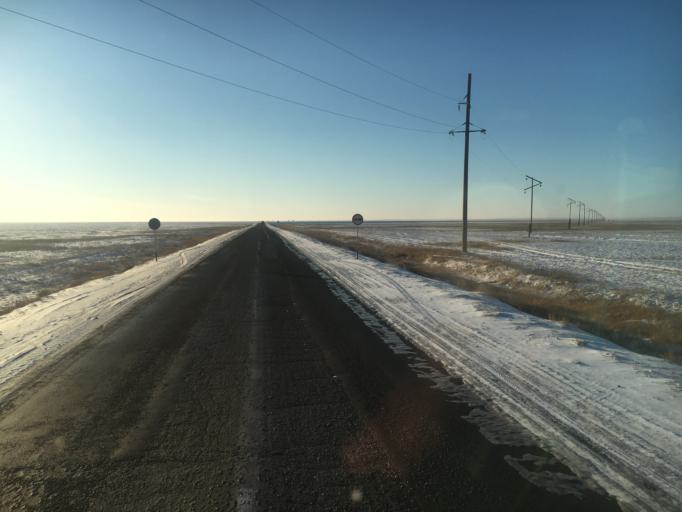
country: KZ
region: Aqtoebe
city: Khromtau
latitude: 50.1177
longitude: 58.9451
